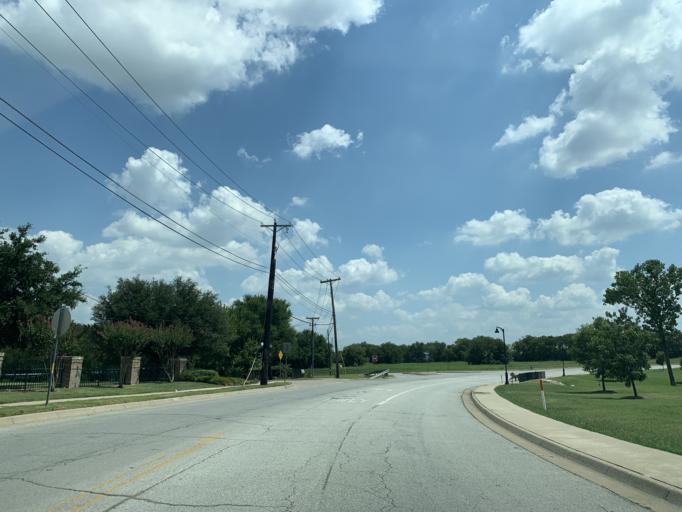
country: US
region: Texas
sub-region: Tarrant County
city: Watauga
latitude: 32.8349
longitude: -97.2725
